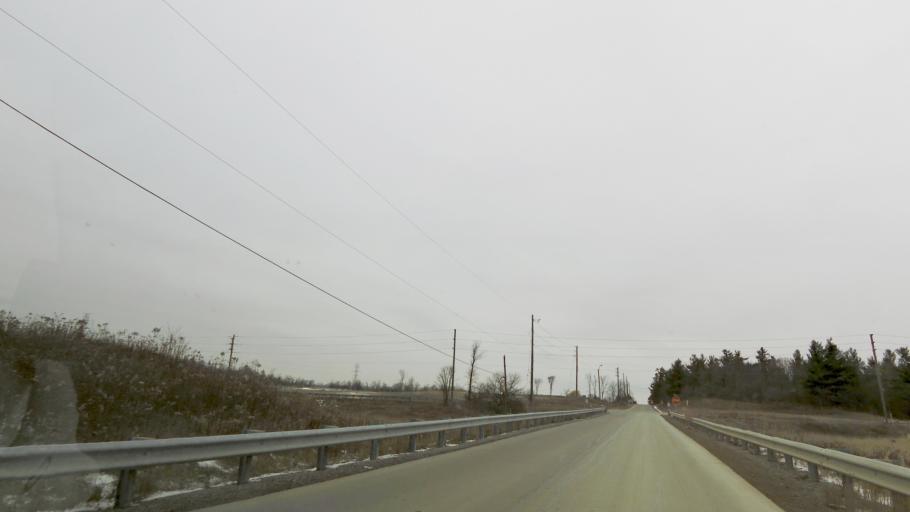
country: CA
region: Ontario
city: Vaughan
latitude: 43.8700
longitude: -79.6185
